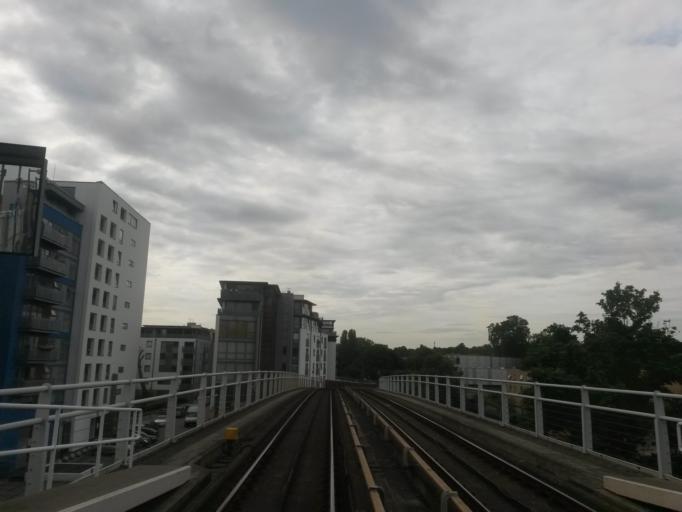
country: GB
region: England
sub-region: Greater London
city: Catford
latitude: 51.4739
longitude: -0.0224
